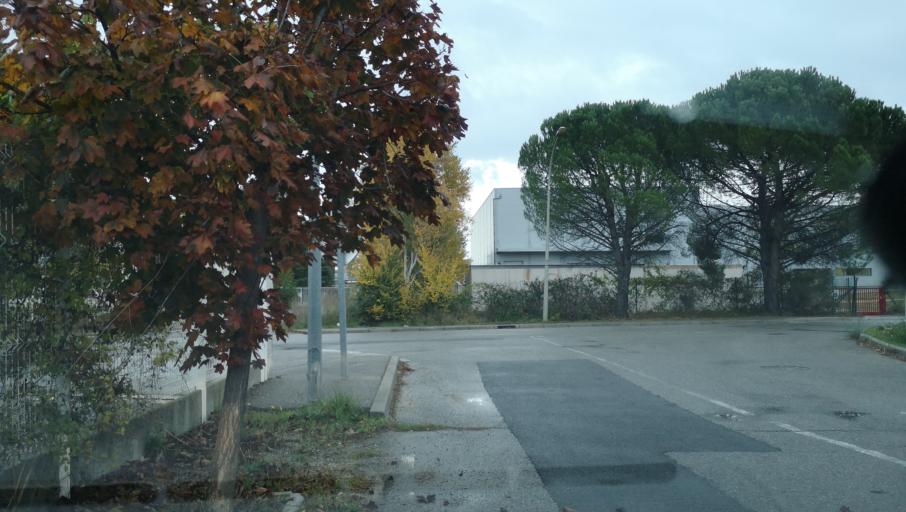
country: FR
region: Provence-Alpes-Cote d'Azur
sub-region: Departement des Bouches-du-Rhone
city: Rousset
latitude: 43.4728
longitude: 5.6090
